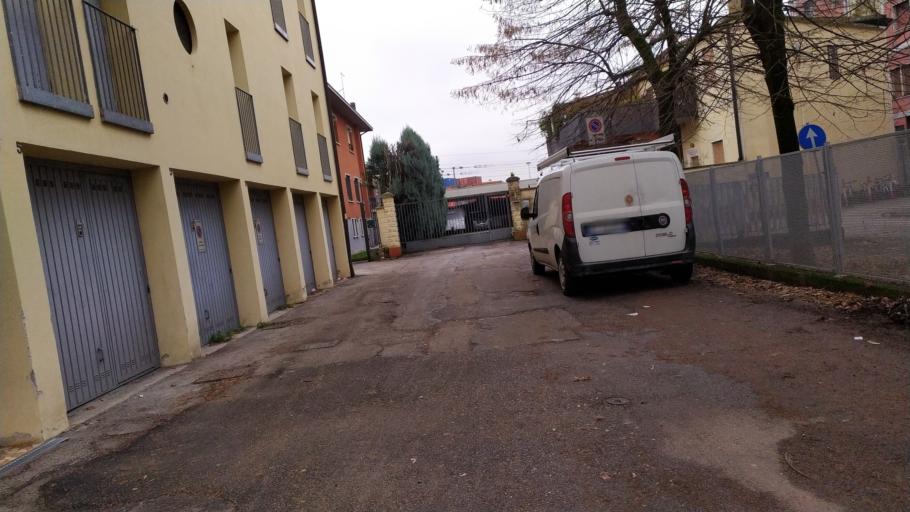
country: IT
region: Veneto
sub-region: Provincia di Vicenza
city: Vicenza
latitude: 45.5382
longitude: 11.5176
